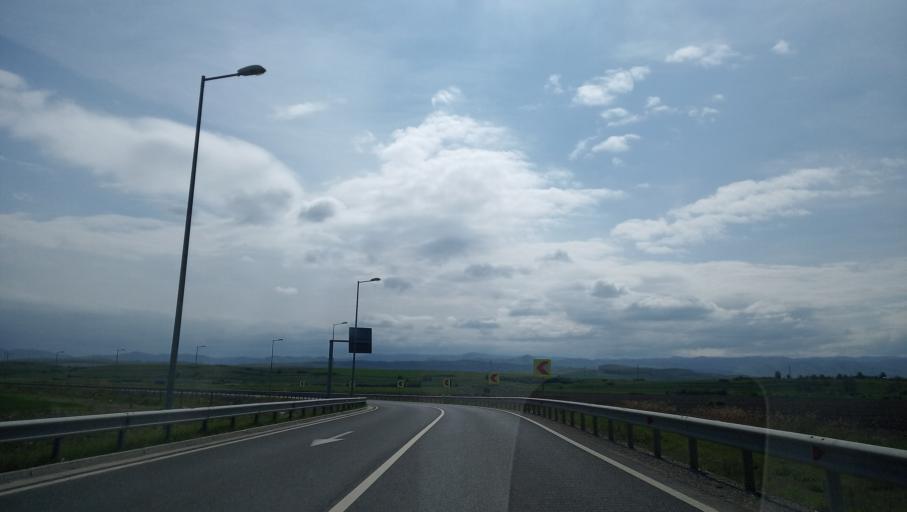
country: RO
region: Hunedoara
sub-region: Comuna Romos
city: Romos
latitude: 45.8881
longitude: 23.2566
